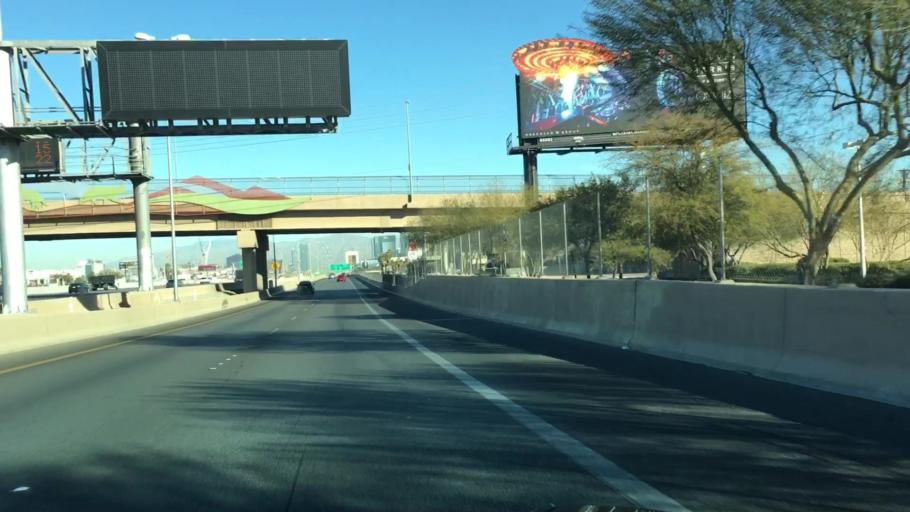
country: US
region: Nevada
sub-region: Clark County
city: Paradise
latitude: 36.0702
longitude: -115.1803
